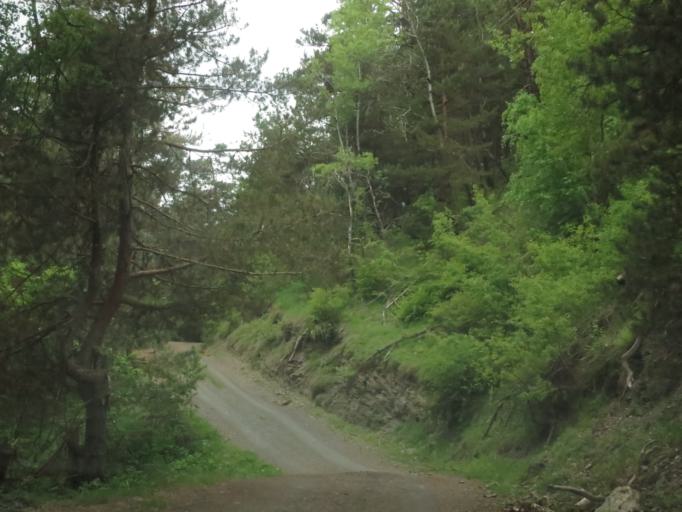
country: RU
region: Chechnya
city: Itum-Kali
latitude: 42.3611
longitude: 45.6568
